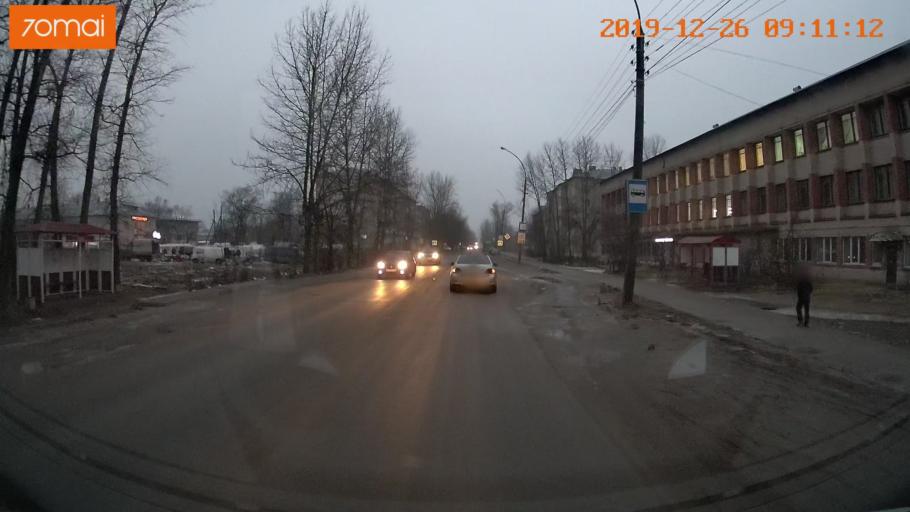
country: RU
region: Vologda
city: Gryazovets
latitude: 58.8748
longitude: 40.2525
